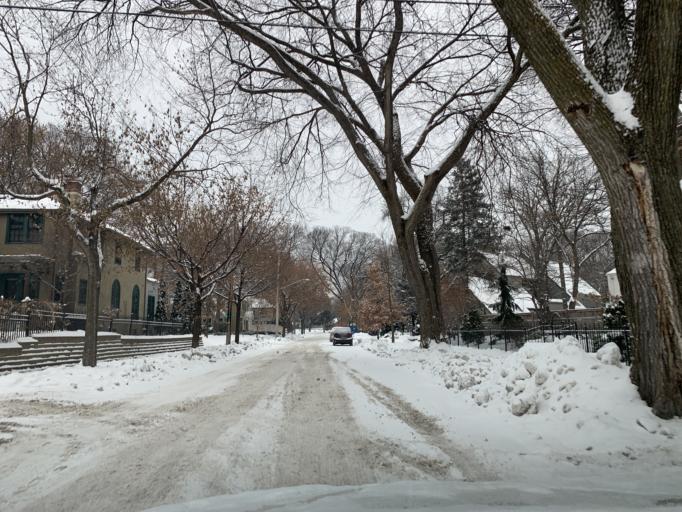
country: US
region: Minnesota
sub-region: Hennepin County
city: Saint Louis Park
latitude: 44.9513
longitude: -93.3283
